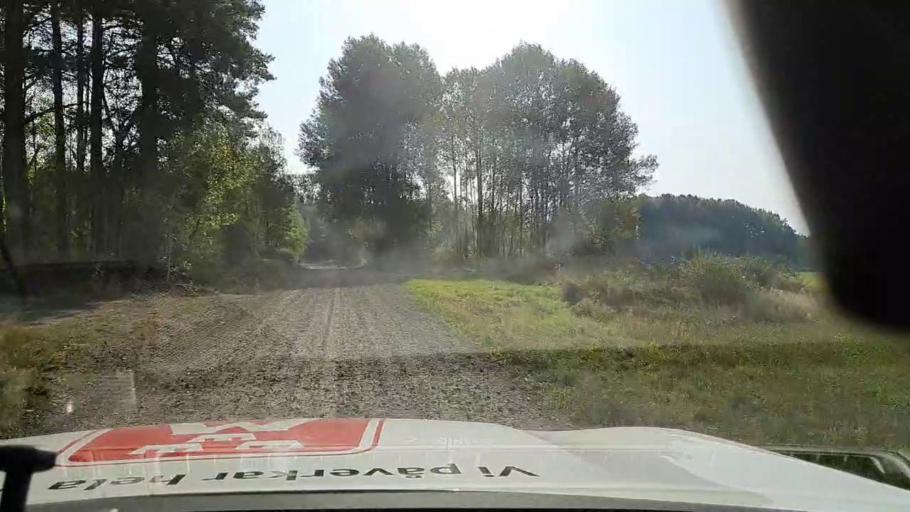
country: SE
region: Vaestmanland
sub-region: Kungsors Kommun
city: Kungsoer
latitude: 59.3499
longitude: 16.1653
